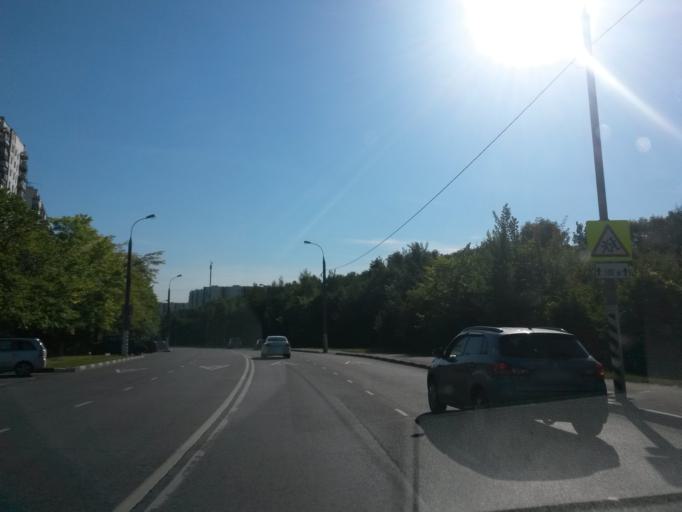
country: RU
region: Moscow
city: Yasenevo
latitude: 55.6123
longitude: 37.5283
